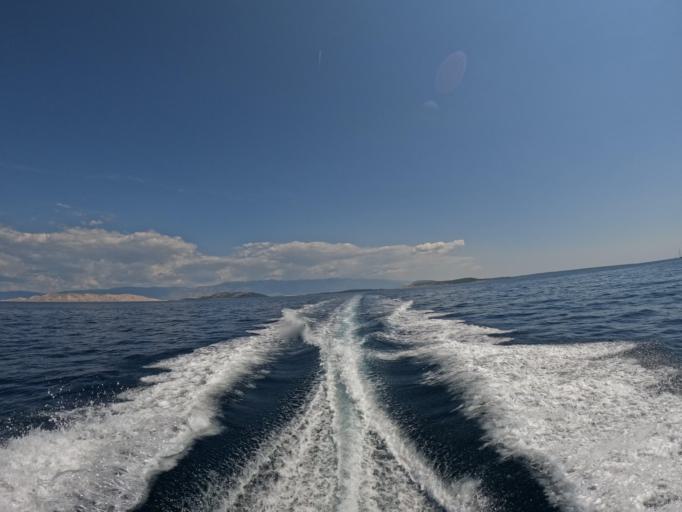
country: HR
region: Primorsko-Goranska
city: Lopar
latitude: 44.8839
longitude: 14.6452
